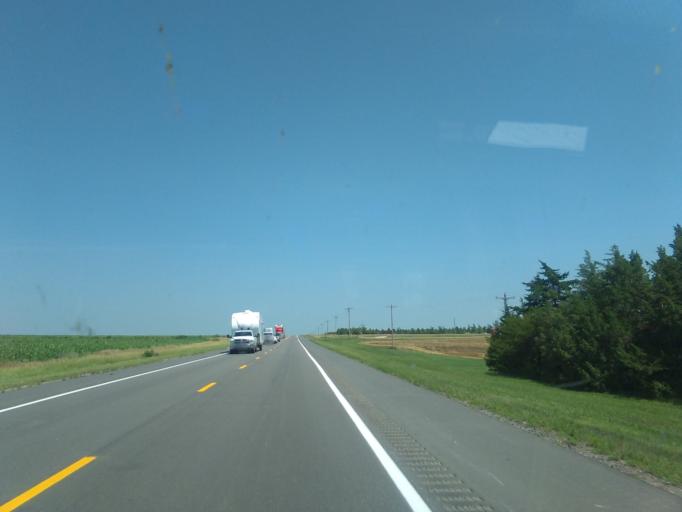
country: US
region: Nebraska
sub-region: Red Willow County
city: McCook
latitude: 40.3017
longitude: -100.6495
